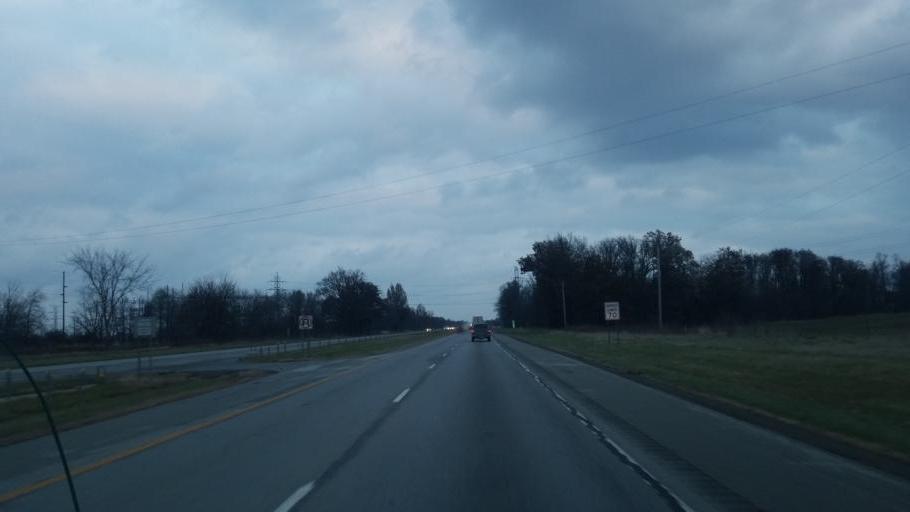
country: US
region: Ohio
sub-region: Allen County
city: Lima
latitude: 40.7957
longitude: -84.0326
